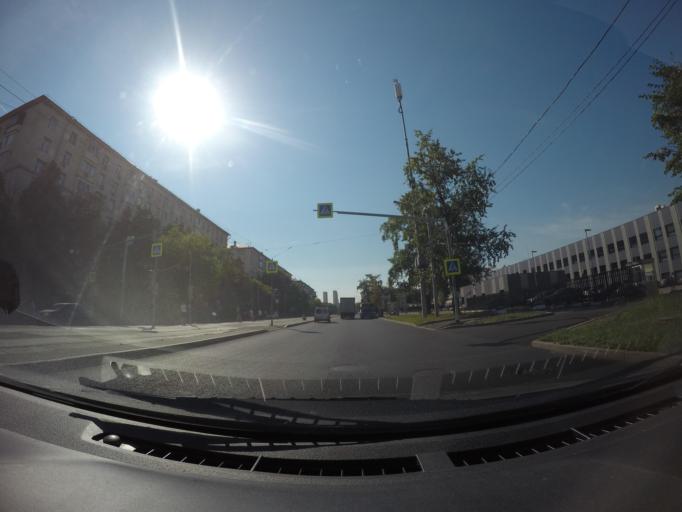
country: RU
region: Moscow
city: Lefortovo
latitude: 55.7703
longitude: 37.7278
